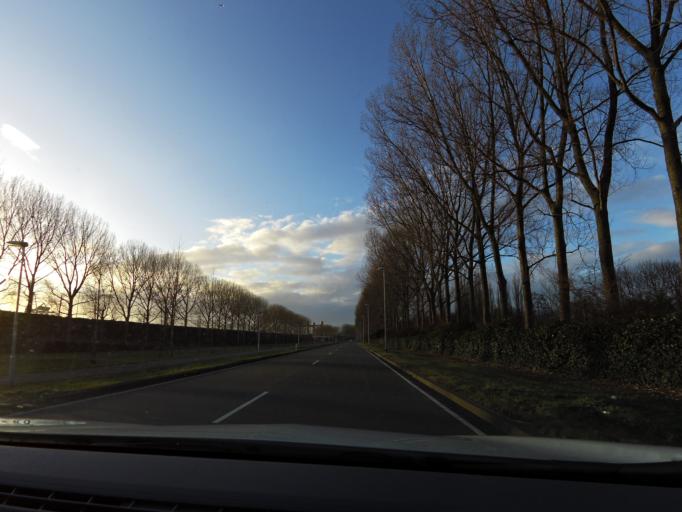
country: NL
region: South Holland
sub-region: Gemeente Maassluis
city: Maassluis
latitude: 51.8996
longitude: 4.2430
